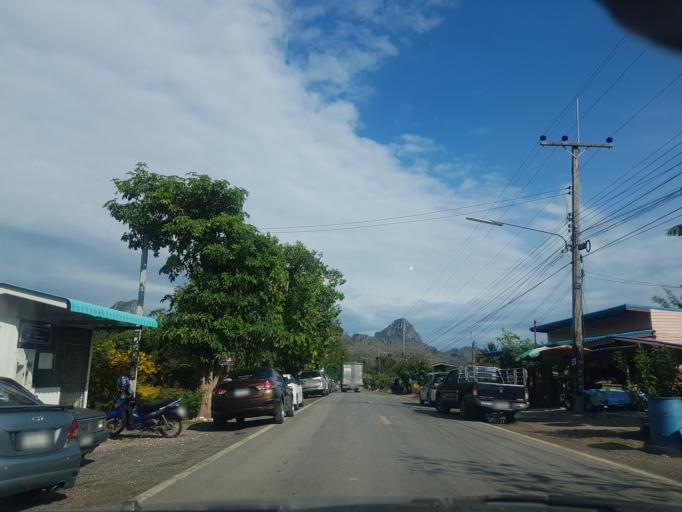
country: TH
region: Sara Buri
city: Phra Phutthabat
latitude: 14.8042
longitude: 100.7526
